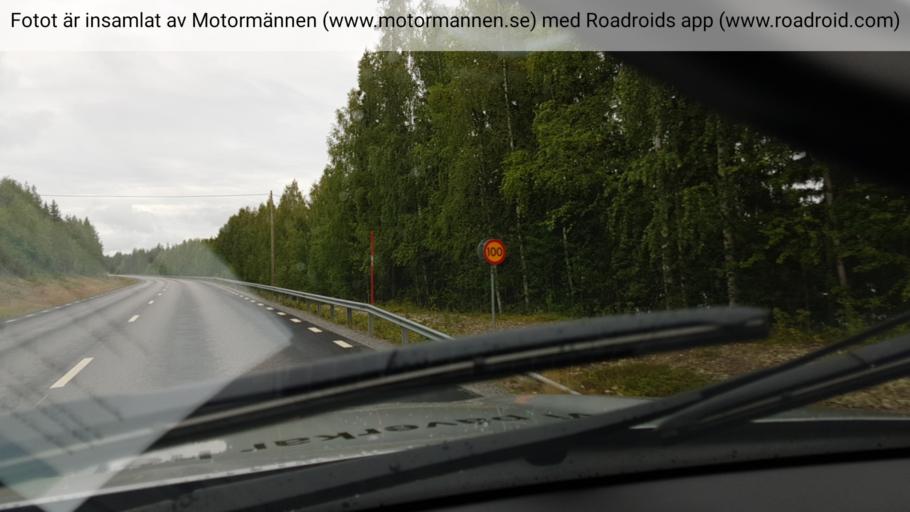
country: SE
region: Norrbotten
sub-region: Alvsbyns Kommun
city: AElvsbyn
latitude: 66.2971
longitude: 20.8114
